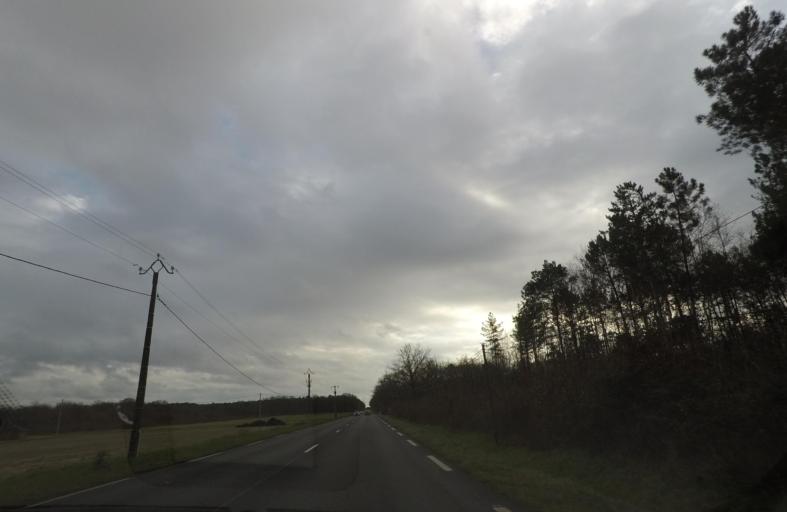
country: FR
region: Centre
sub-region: Departement du Loir-et-Cher
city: Mur-de-Sologne
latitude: 47.4234
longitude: 1.5822
